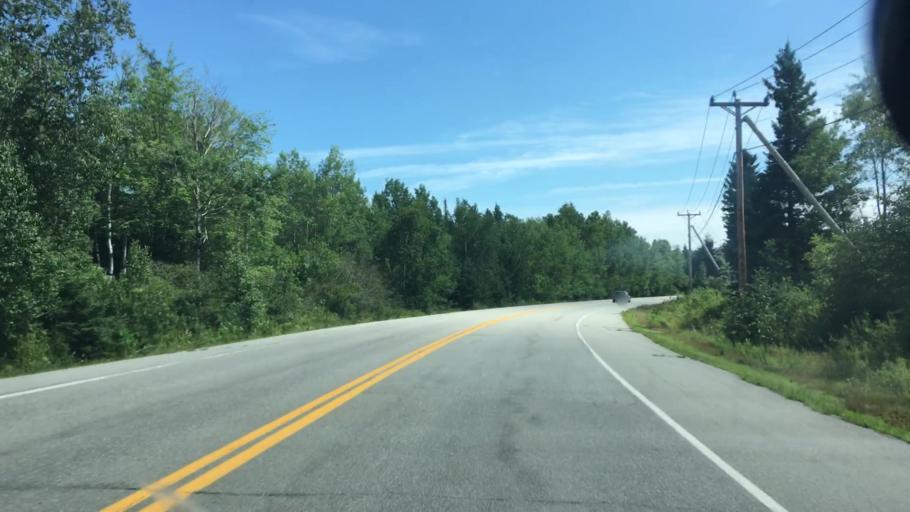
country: US
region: Maine
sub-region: Washington County
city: Eastport
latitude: 44.9372
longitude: -67.0275
